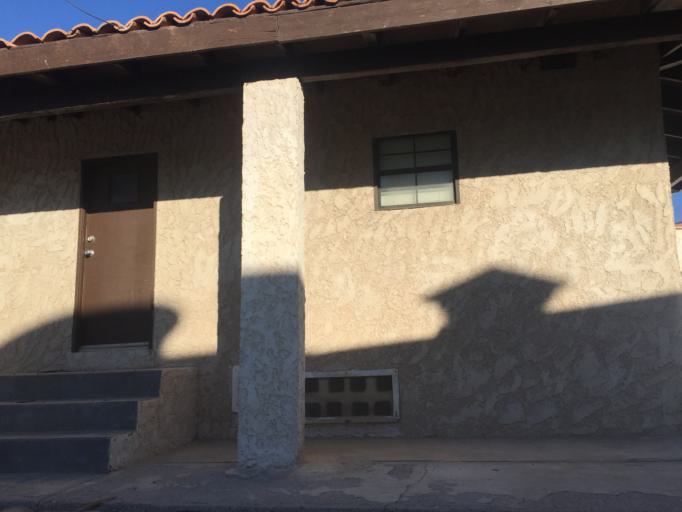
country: MX
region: Sonora
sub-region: Puerto Penasco
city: Puerto Penasco
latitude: 31.2917
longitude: -113.5056
